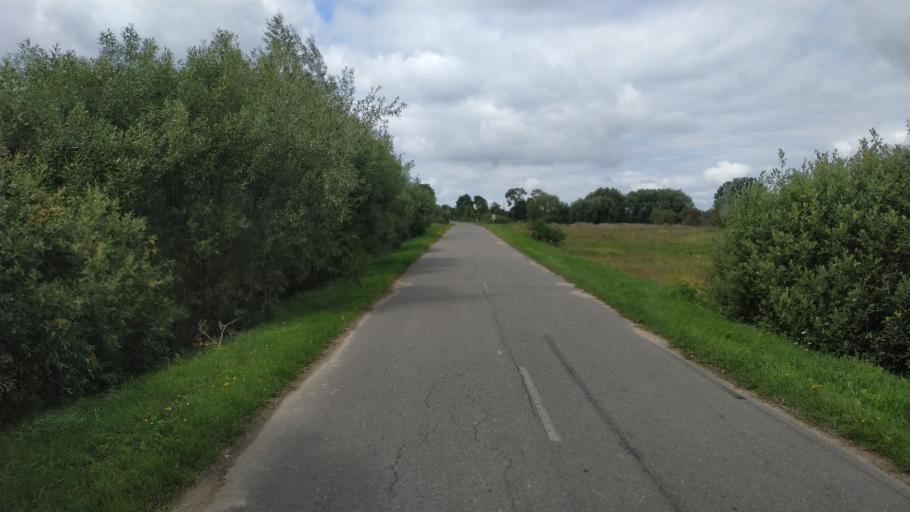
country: BY
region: Mogilev
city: Chavusy
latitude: 53.7797
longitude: 30.8919
